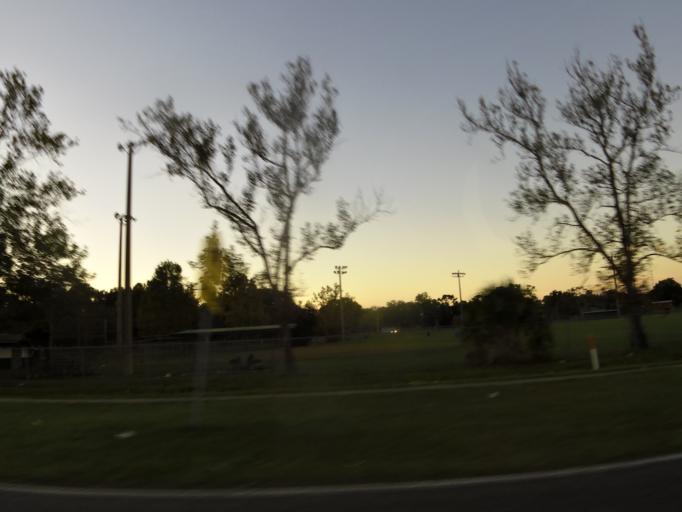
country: US
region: Florida
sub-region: Duval County
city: Jacksonville
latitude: 30.3097
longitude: -81.7430
